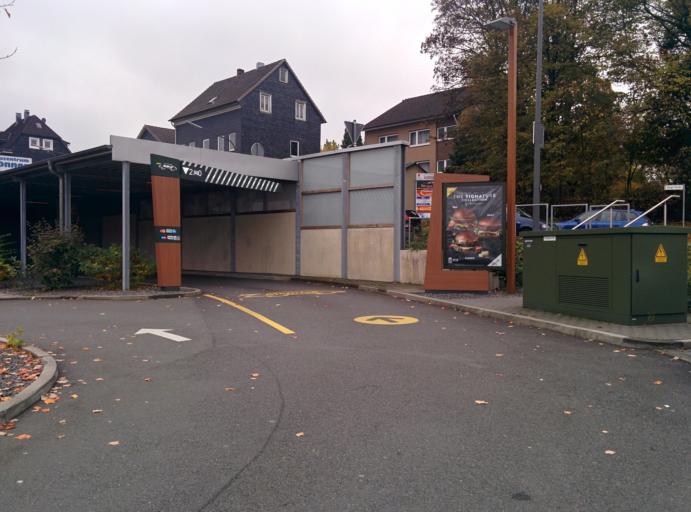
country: DE
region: North Rhine-Westphalia
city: Wermelskirchen
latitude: 51.1370
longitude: 7.1995
